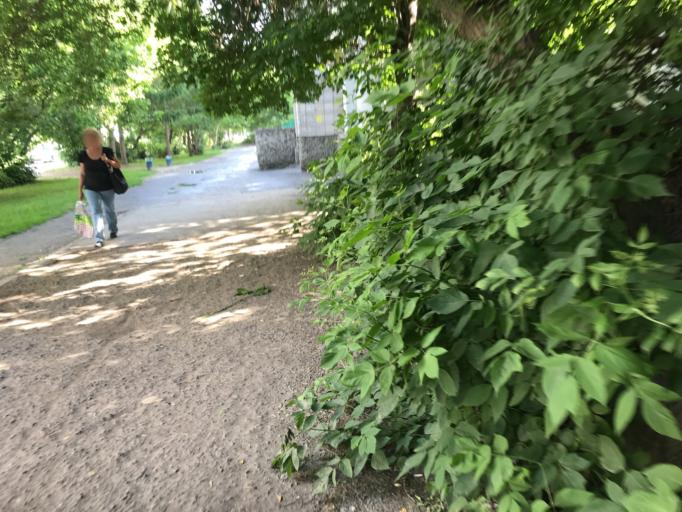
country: RU
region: Novosibirsk
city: Krasnoobsk
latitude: 54.9347
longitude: 82.9084
